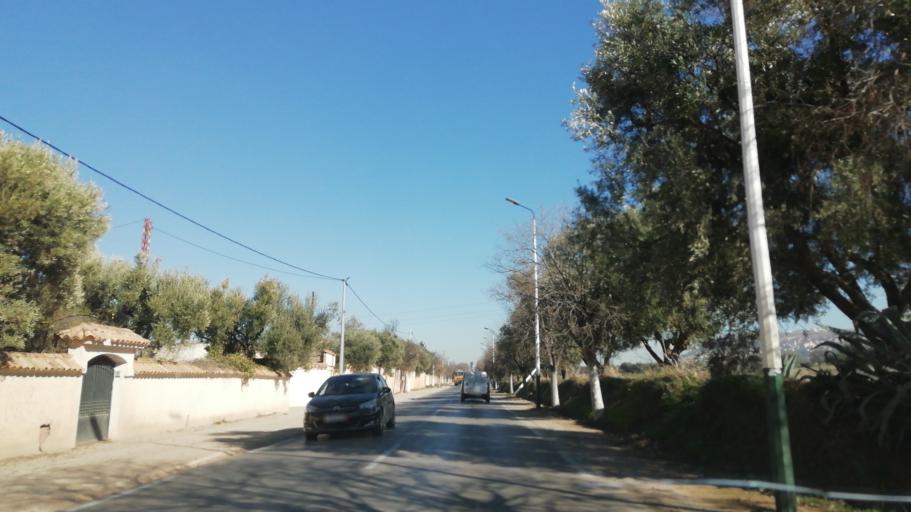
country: DZ
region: Tlemcen
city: Mansoura
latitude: 34.8646
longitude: -1.3550
